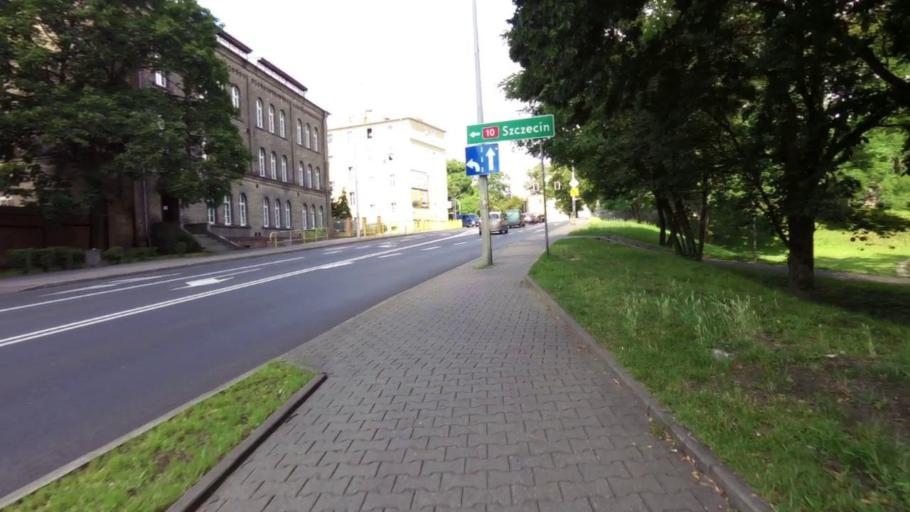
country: PL
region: West Pomeranian Voivodeship
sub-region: Powiat stargardzki
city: Stargard Szczecinski
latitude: 53.3345
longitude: 15.0423
